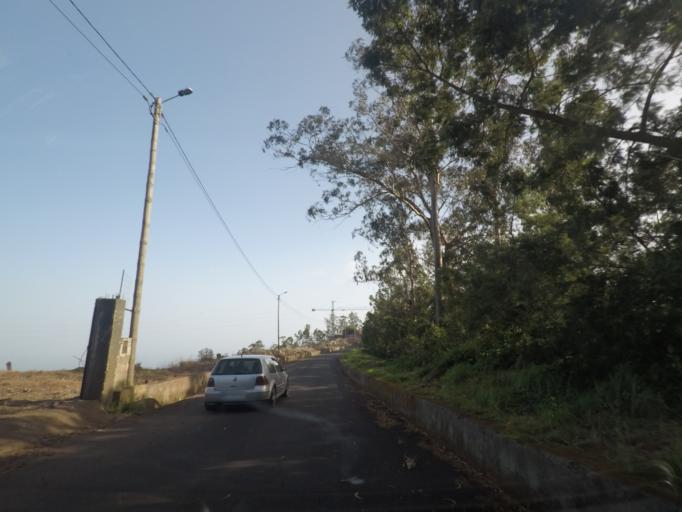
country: PT
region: Madeira
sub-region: Ribeira Brava
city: Campanario
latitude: 32.6695
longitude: -17.0030
